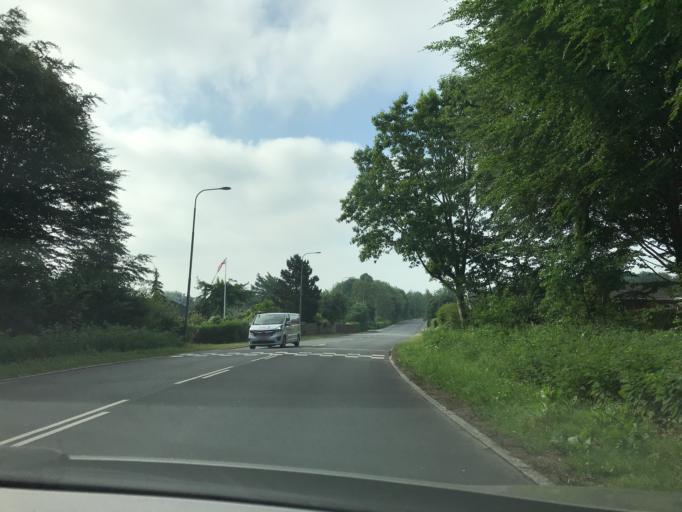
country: DK
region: South Denmark
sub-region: Odense Kommune
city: Bellinge
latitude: 55.3761
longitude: 10.3413
